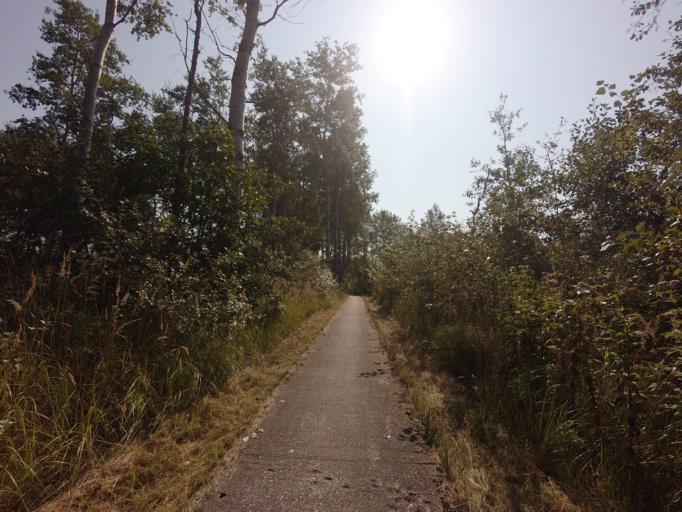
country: NL
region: Groningen
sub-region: Gemeente De Marne
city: Ulrum
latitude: 53.3928
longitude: 6.2548
